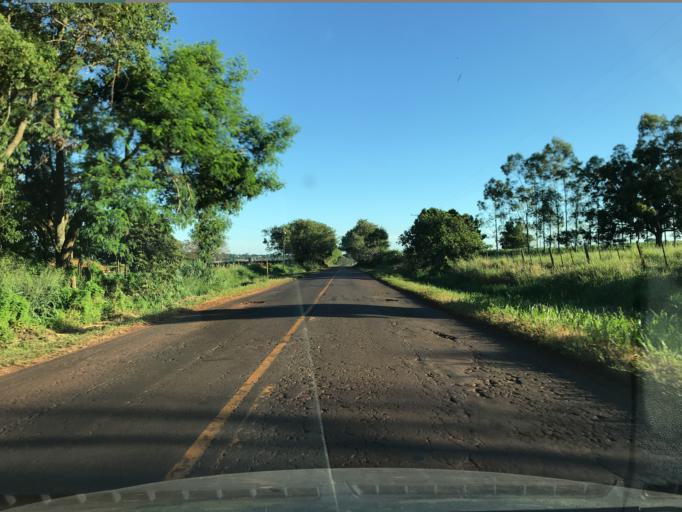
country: BR
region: Parana
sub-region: Ipora
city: Ipora
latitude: -24.0884
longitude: -53.8351
